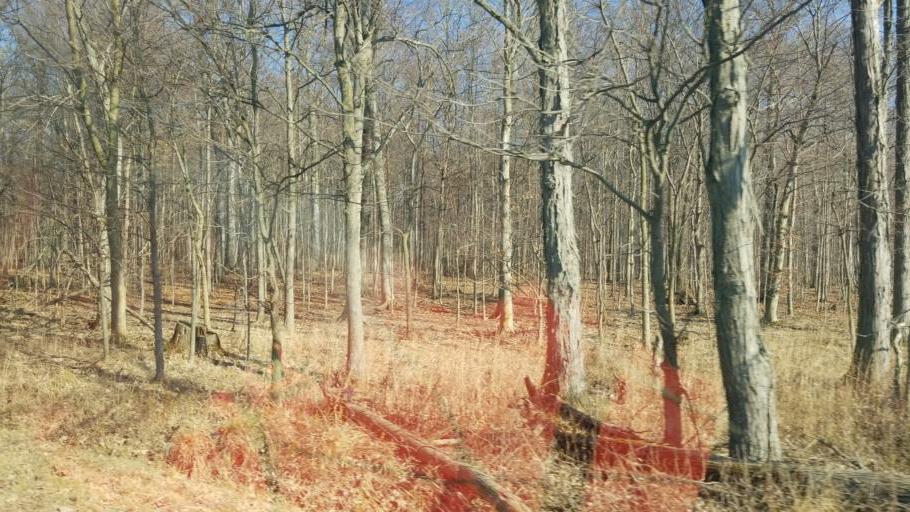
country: US
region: Ohio
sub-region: Seneca County
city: Tiffin
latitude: 41.0173
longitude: -83.0741
